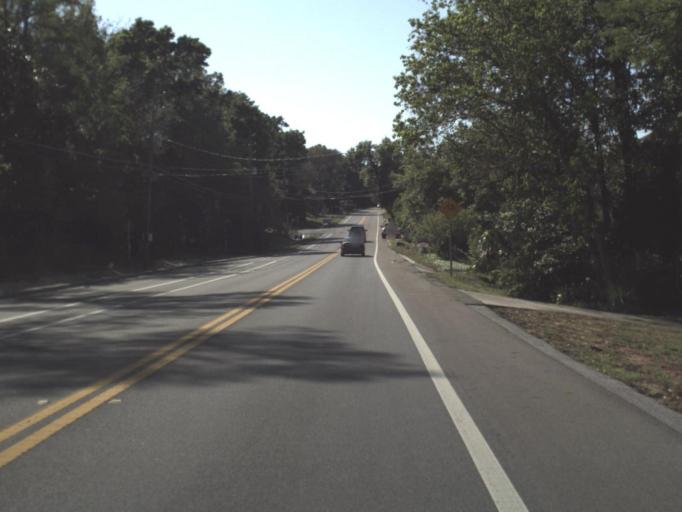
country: US
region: Florida
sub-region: Escambia County
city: Ferry Pass
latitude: 30.5205
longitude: -87.1750
